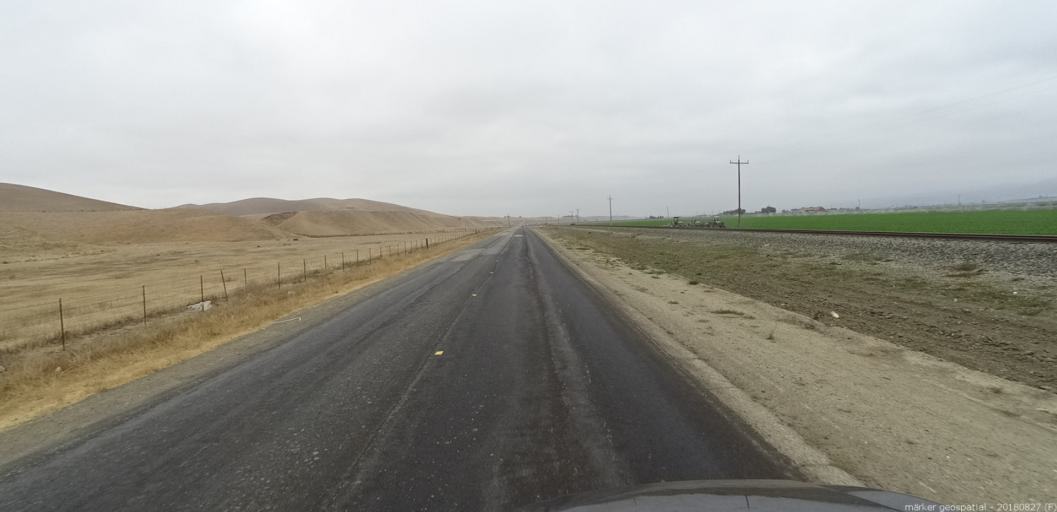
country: US
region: California
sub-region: Monterey County
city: Greenfield
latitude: 36.3072
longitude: -121.1652
